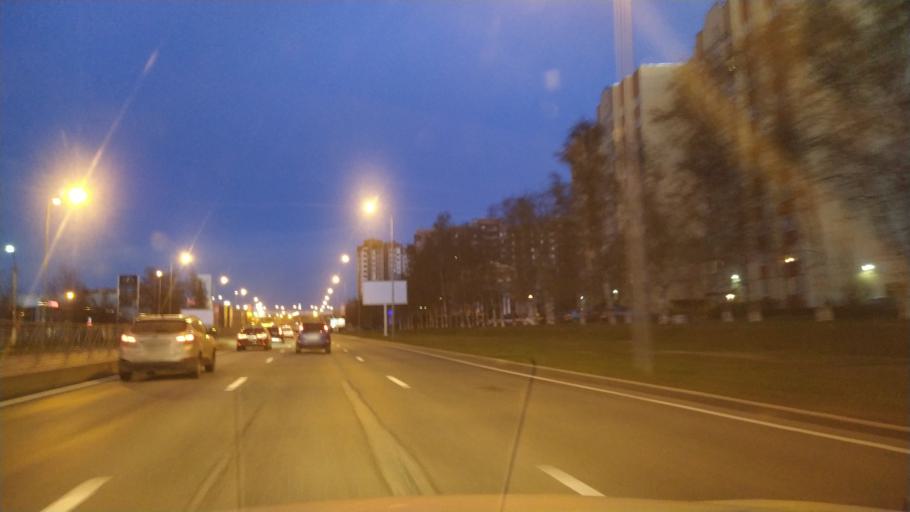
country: RU
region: St.-Petersburg
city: Staraya Derevnya
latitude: 59.9905
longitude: 30.2205
